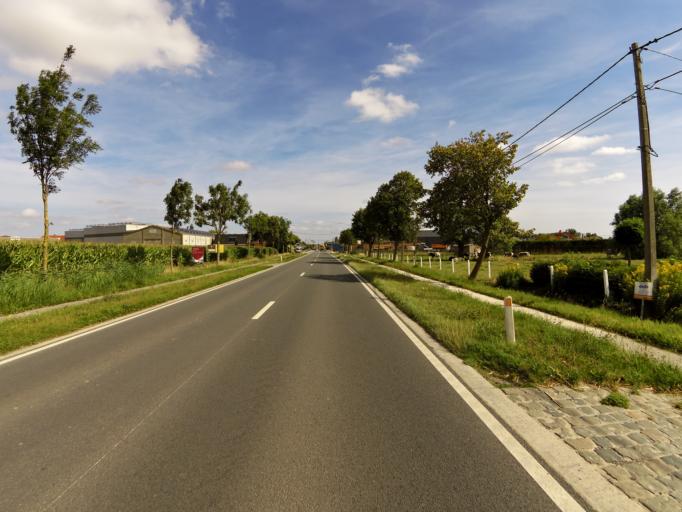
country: BE
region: Flanders
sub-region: Provincie West-Vlaanderen
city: Diksmuide
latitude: 50.9545
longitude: 2.8654
